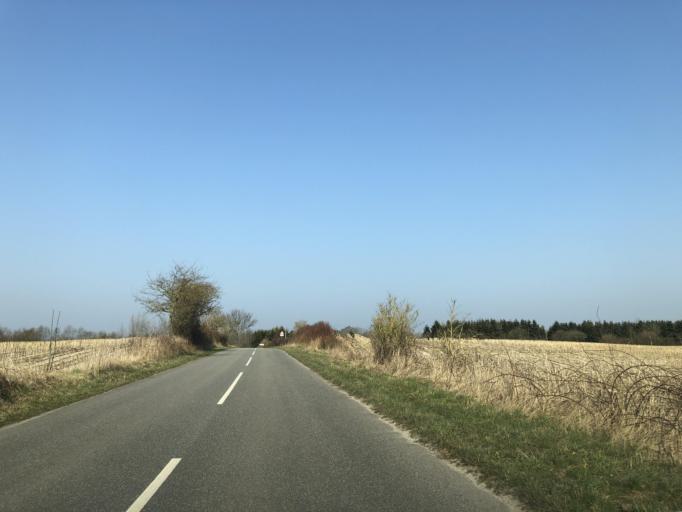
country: DK
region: South Denmark
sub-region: Sonderborg Kommune
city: Nordborg
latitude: 55.0733
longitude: 9.7312
